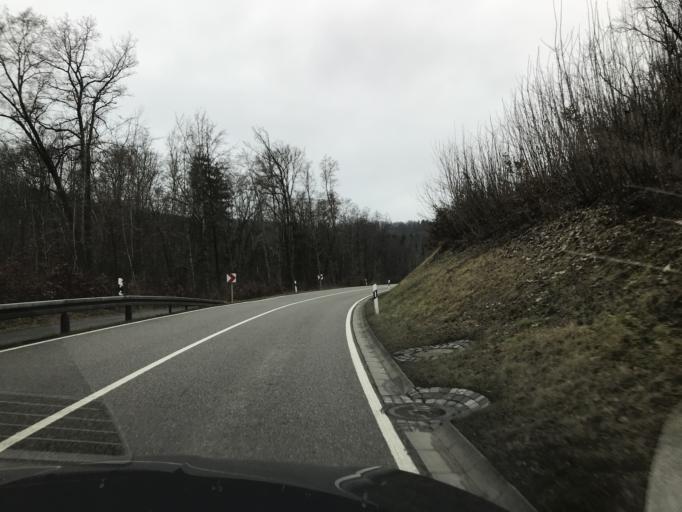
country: DE
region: Baden-Wuerttemberg
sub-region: Regierungsbezirk Stuttgart
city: Wolfschlugen
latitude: 48.6370
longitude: 9.3033
